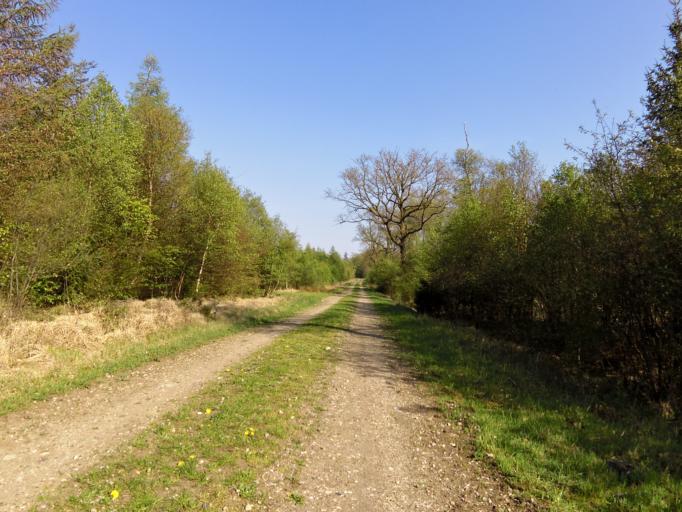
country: DK
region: South Denmark
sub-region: Tonder Kommune
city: Toftlund
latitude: 55.1951
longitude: 8.9439
